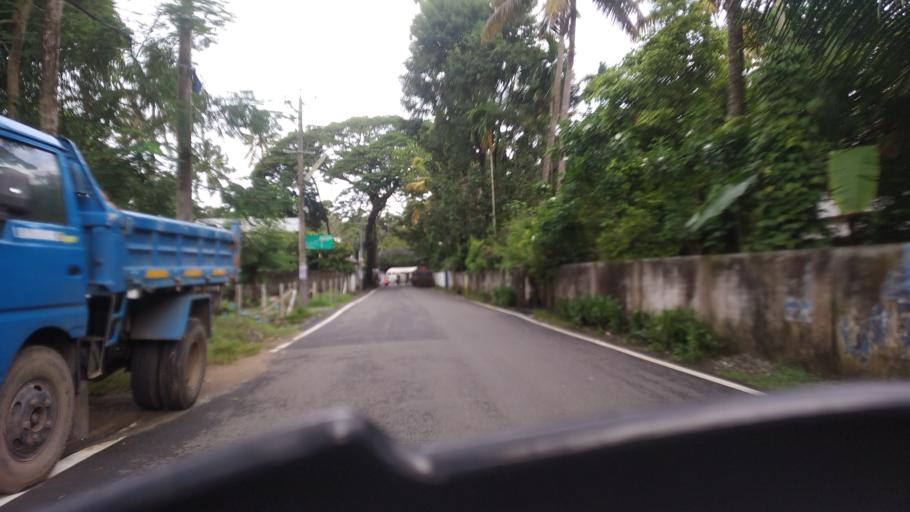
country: IN
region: Kerala
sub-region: Ernakulam
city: Elur
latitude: 10.1022
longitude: 76.2032
